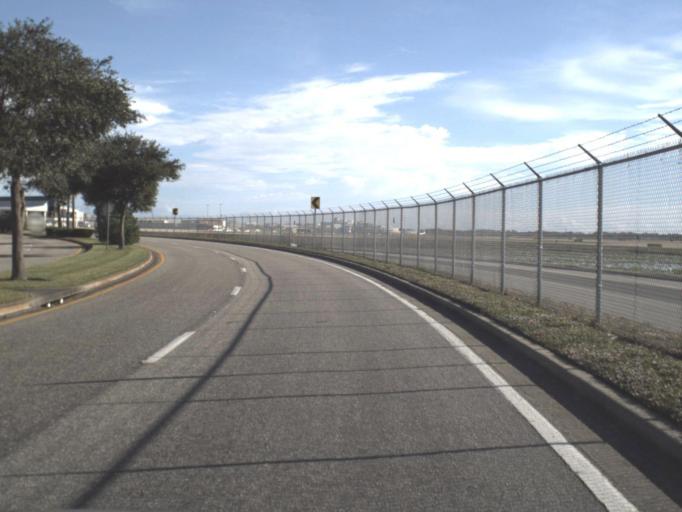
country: US
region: Florida
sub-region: Volusia County
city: Daytona Beach
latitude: 29.1804
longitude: -81.0644
